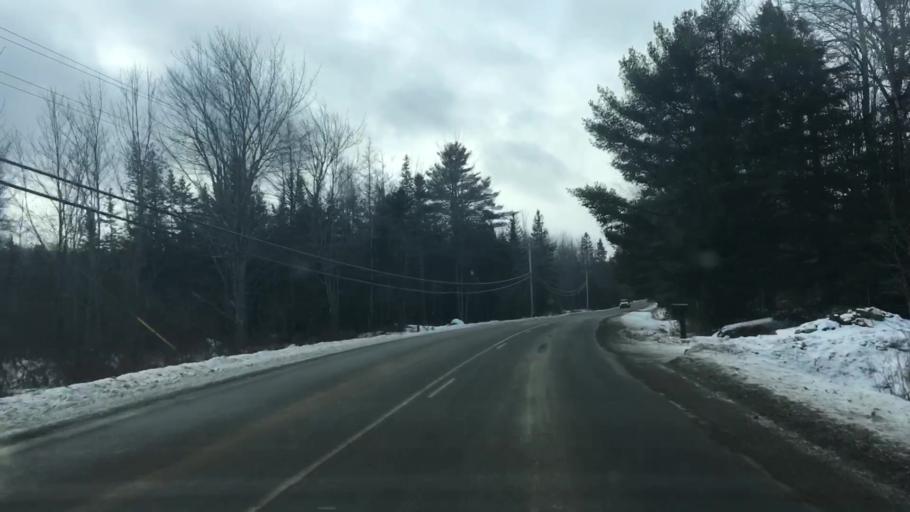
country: US
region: Maine
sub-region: Washington County
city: Calais
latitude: 45.0420
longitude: -67.3281
